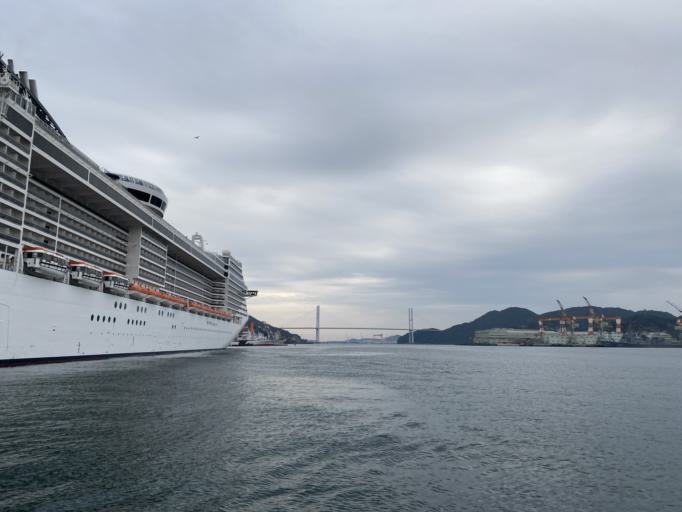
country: JP
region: Nagasaki
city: Nagasaki-shi
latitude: 32.7386
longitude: 129.8674
